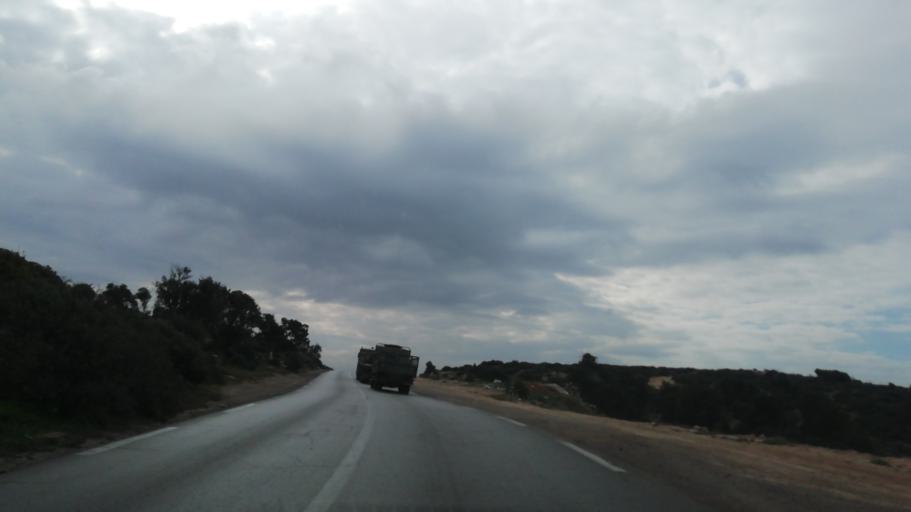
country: DZ
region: Oran
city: Ain el Bya
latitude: 35.7203
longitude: -0.3576
